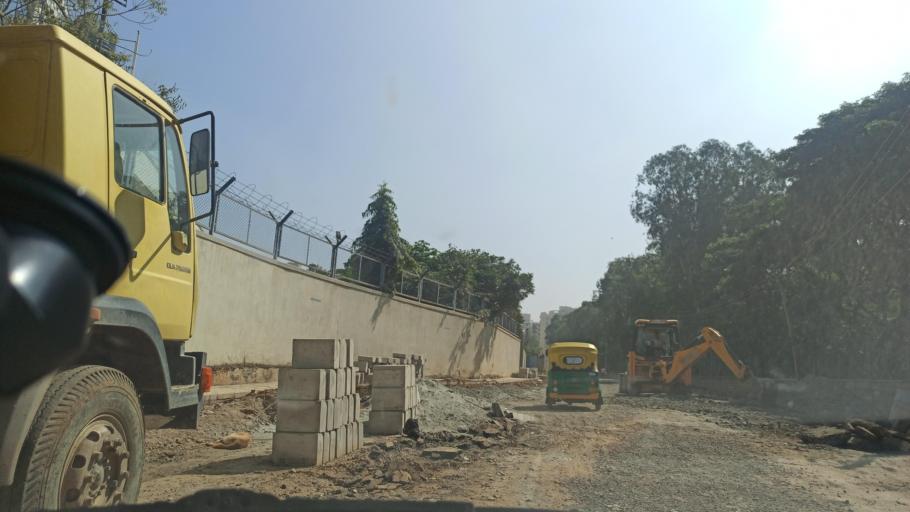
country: IN
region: Karnataka
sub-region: Bangalore Urban
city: Bangalore
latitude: 12.9186
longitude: 77.6861
